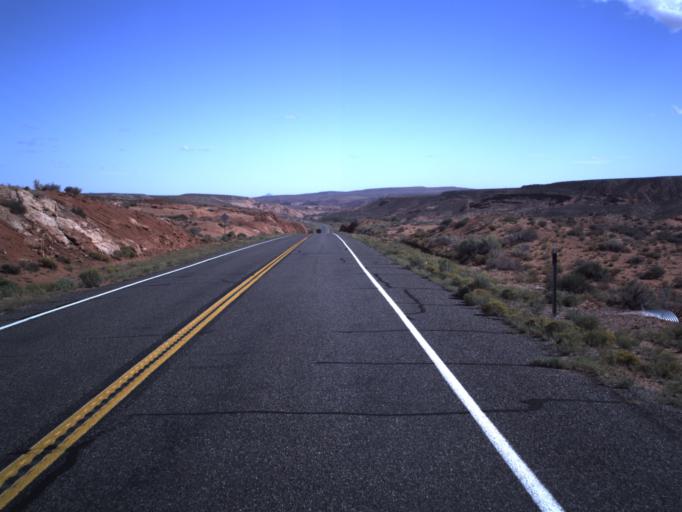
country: US
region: Utah
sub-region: Wayne County
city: Loa
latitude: 38.0666
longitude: -110.6032
